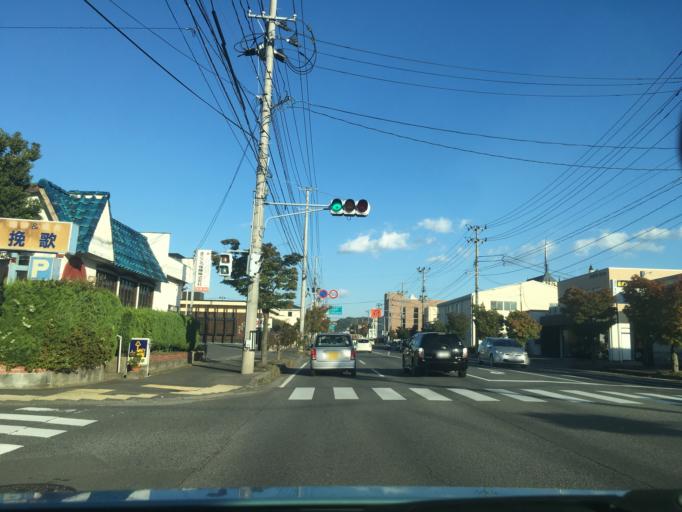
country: JP
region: Fukushima
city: Iwaki
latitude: 37.0478
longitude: 140.8864
